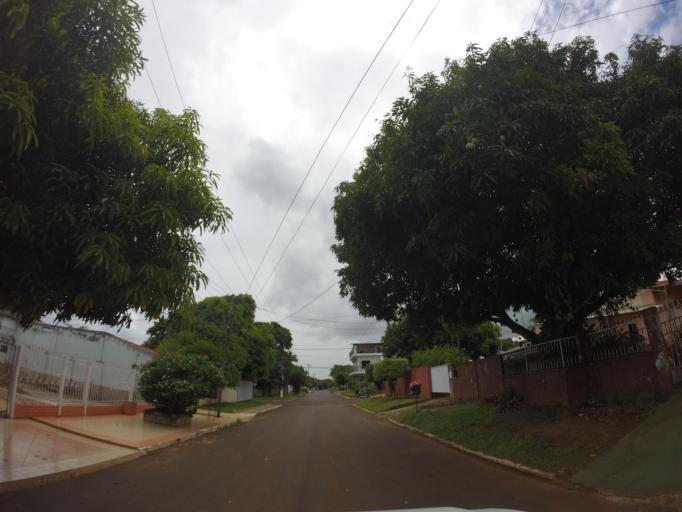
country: PY
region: Alto Parana
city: Ciudad del Este
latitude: -25.4168
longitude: -54.6279
